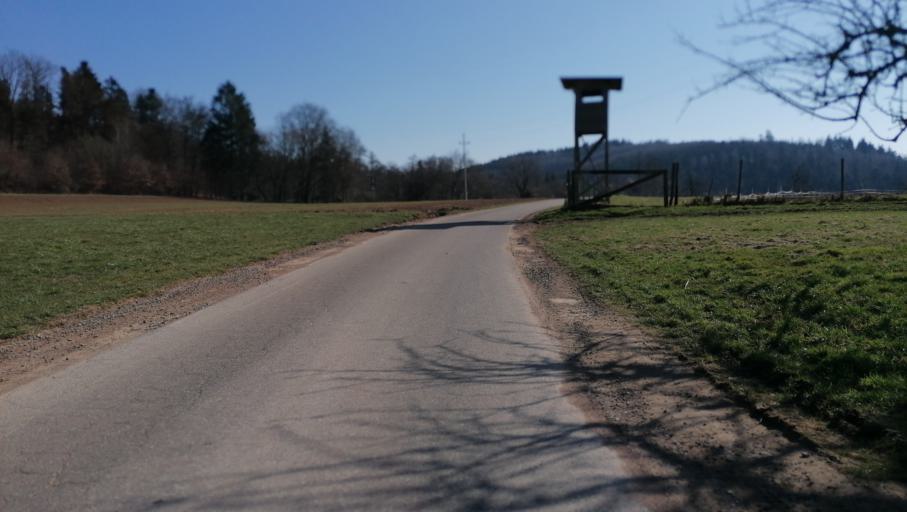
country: CH
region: Aargau
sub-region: Bezirk Rheinfelden
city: Mumpf
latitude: 47.5848
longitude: 7.9191
